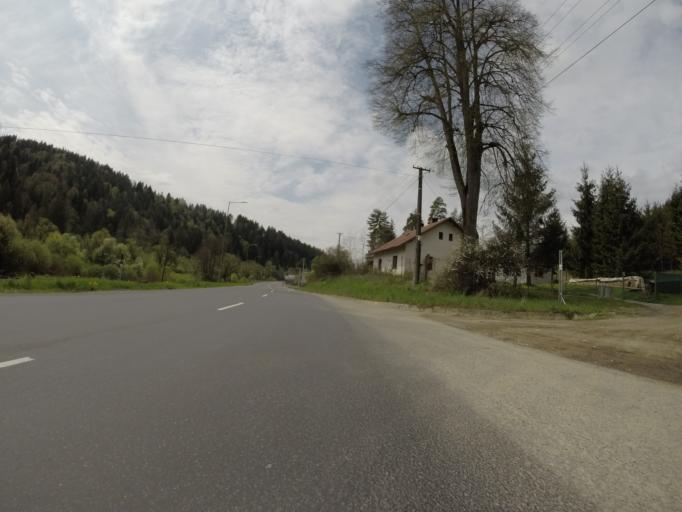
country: SK
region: Banskobystricky
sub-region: Okres Banska Bystrica
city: Brezno
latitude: 48.8224
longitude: 19.6911
